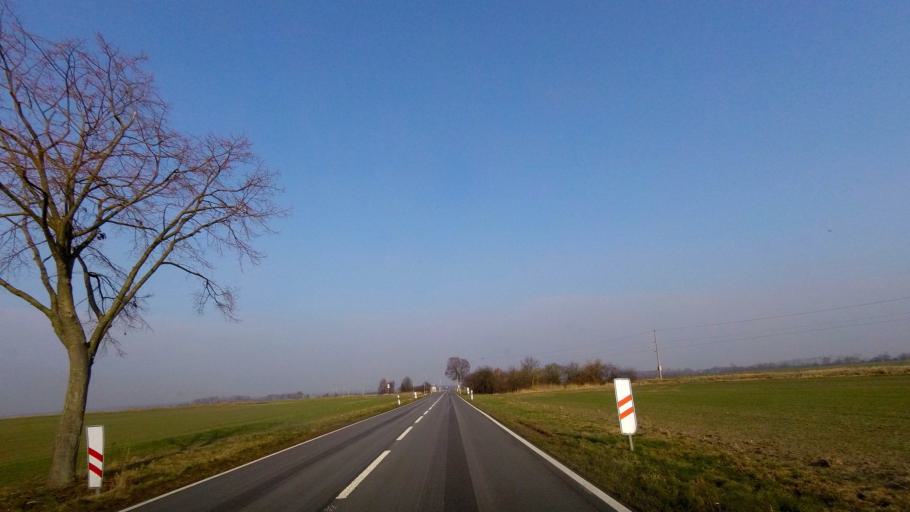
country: DE
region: Brandenburg
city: Juterbog
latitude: 51.9485
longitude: 13.0395
